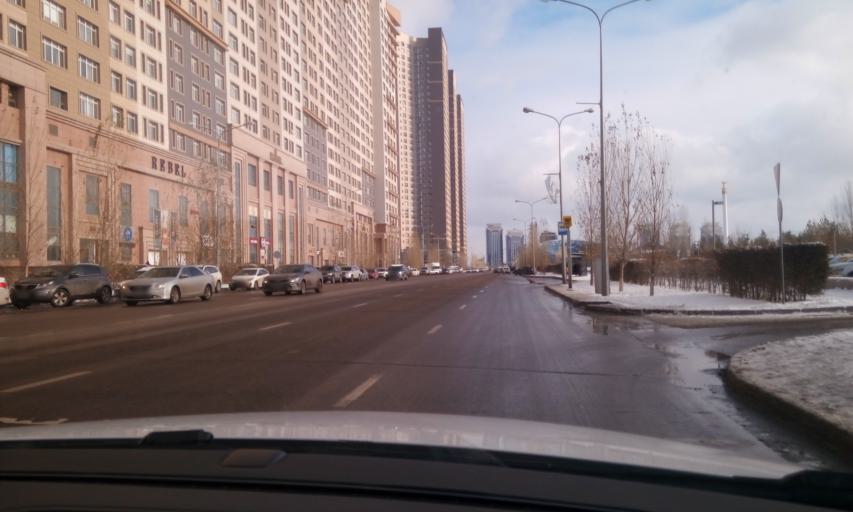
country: KZ
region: Astana Qalasy
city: Astana
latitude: 51.1269
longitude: 71.4606
